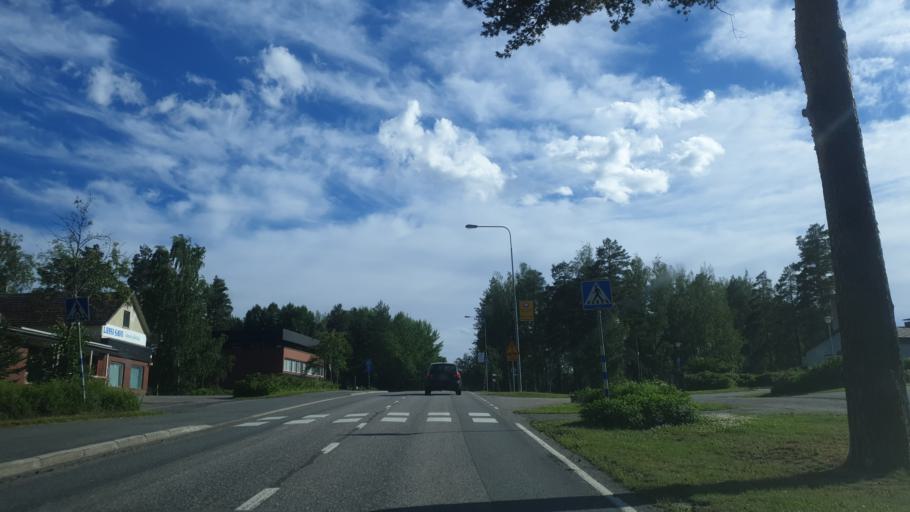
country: FI
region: Southern Savonia
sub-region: Mikkeli
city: Pertunmaa
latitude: 61.5035
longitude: 26.4801
